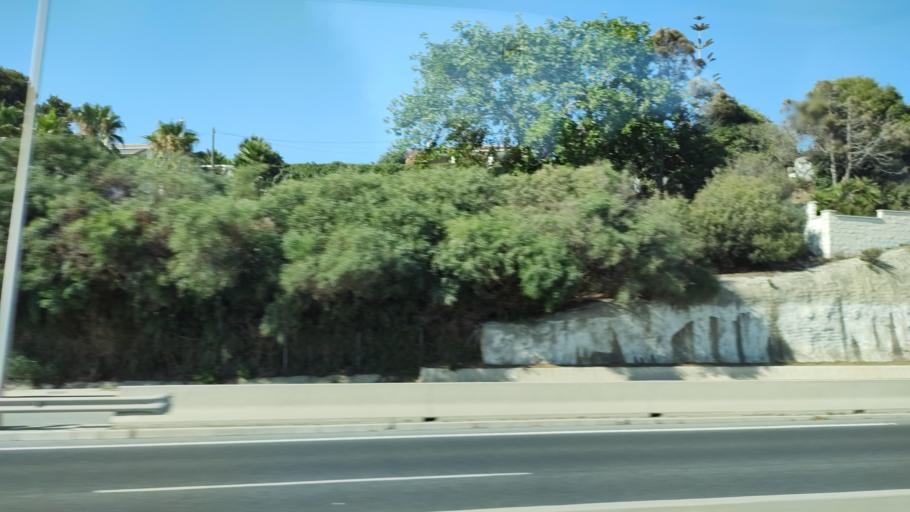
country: ES
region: Andalusia
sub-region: Provincia de Malaga
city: Fuengirola
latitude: 36.5072
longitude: -4.6607
